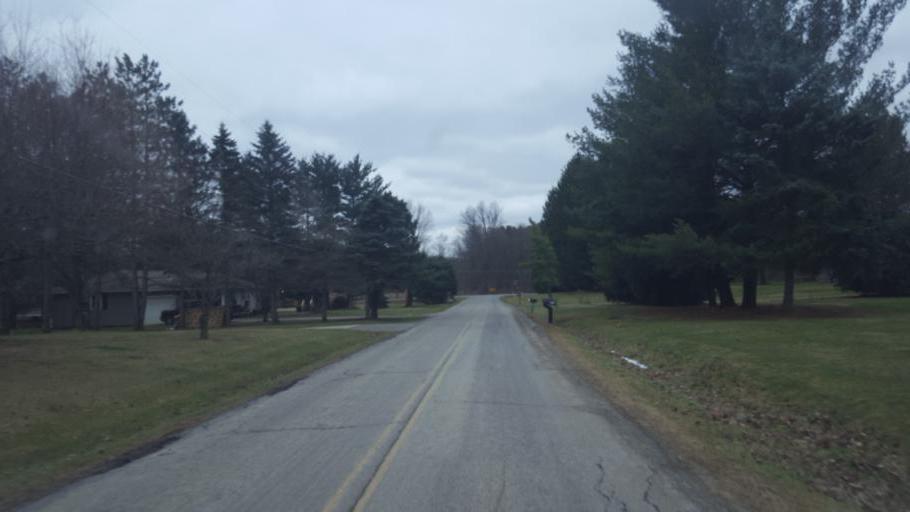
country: US
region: Ohio
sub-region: Crawford County
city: Crestline
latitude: 40.7345
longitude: -82.6981
